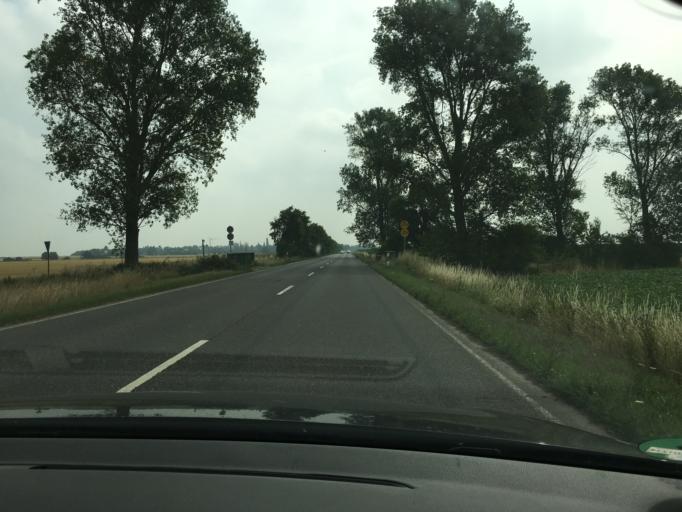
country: DE
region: North Rhine-Westphalia
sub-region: Regierungsbezirk Koln
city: Merzenich
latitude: 50.7938
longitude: 6.5512
